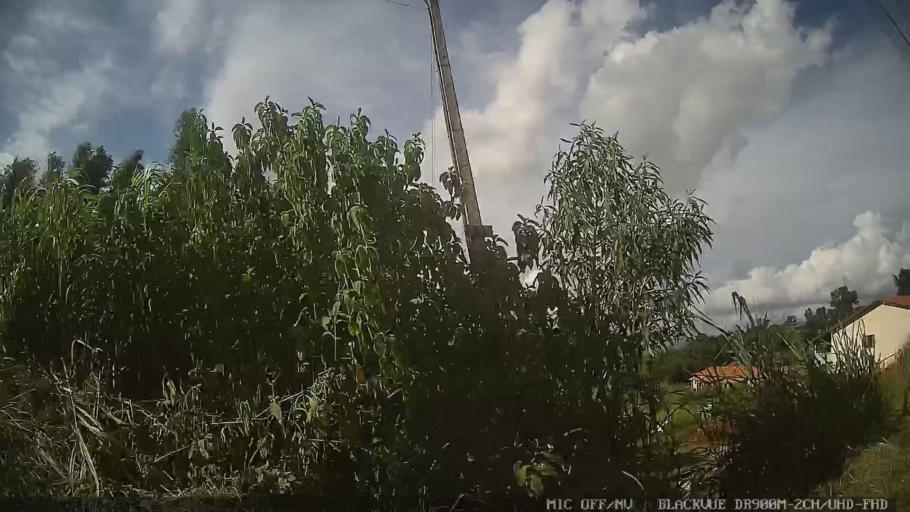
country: BR
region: Sao Paulo
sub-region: Bom Jesus Dos Perdoes
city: Bom Jesus dos Perdoes
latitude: -23.1234
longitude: -46.4872
